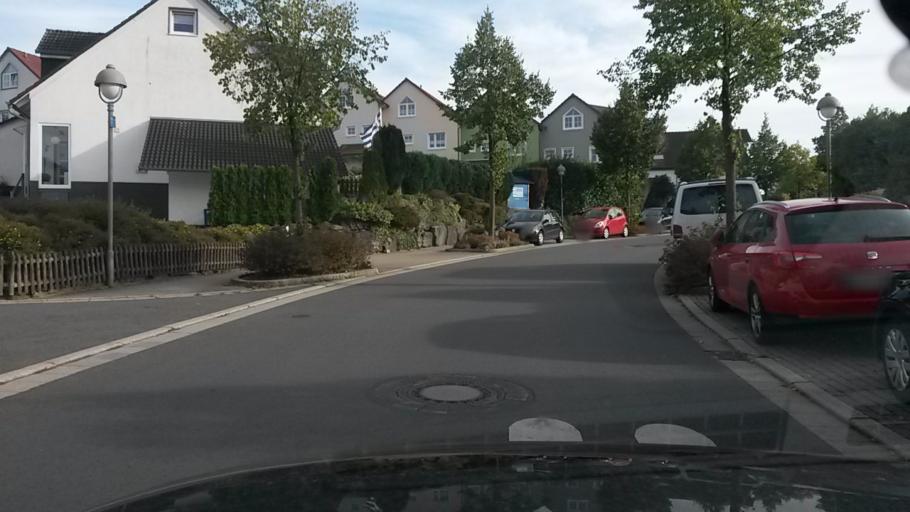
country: DE
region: North Rhine-Westphalia
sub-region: Regierungsbezirk Arnsberg
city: Luedenscheid
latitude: 51.2323
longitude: 7.6451
